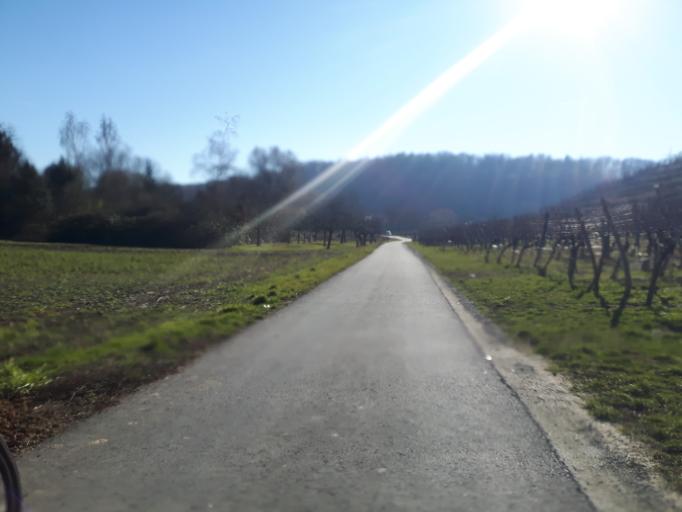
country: DE
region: Baden-Wuerttemberg
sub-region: Regierungsbezirk Stuttgart
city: Lauffen am Neckar
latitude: 49.0687
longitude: 9.1285
